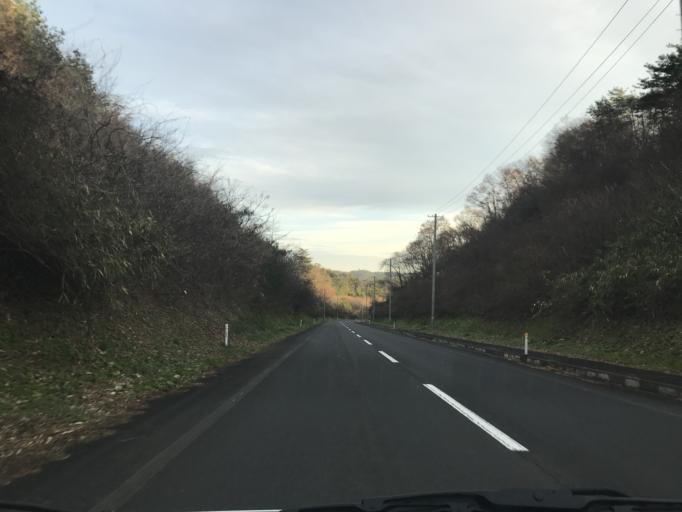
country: JP
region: Iwate
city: Ichinoseki
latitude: 38.9815
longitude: 141.0694
